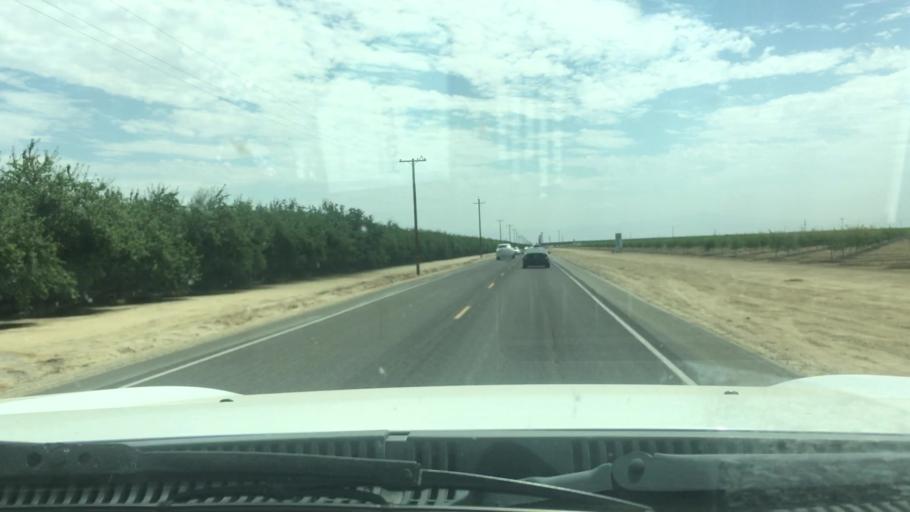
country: US
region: California
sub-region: Kern County
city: Wasco
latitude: 35.5581
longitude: -119.3015
